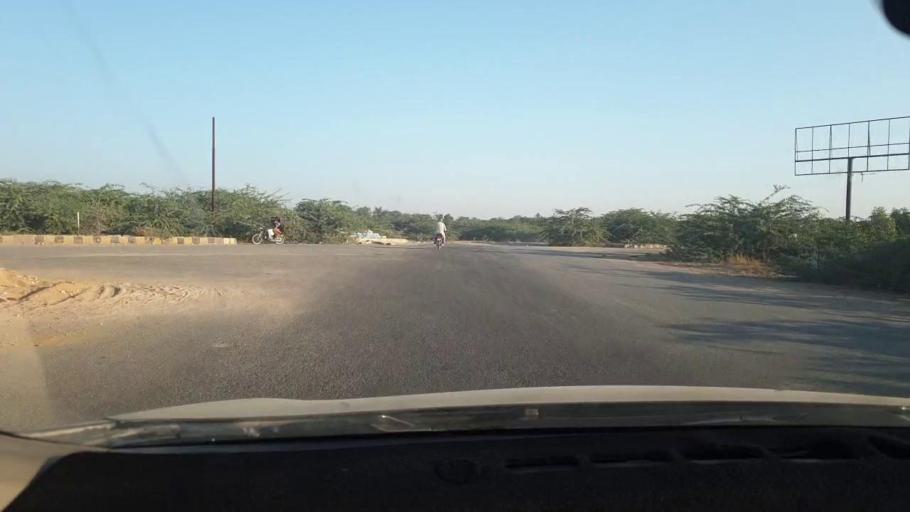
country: PK
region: Sindh
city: Malir Cantonment
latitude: 25.0500
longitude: 67.1817
